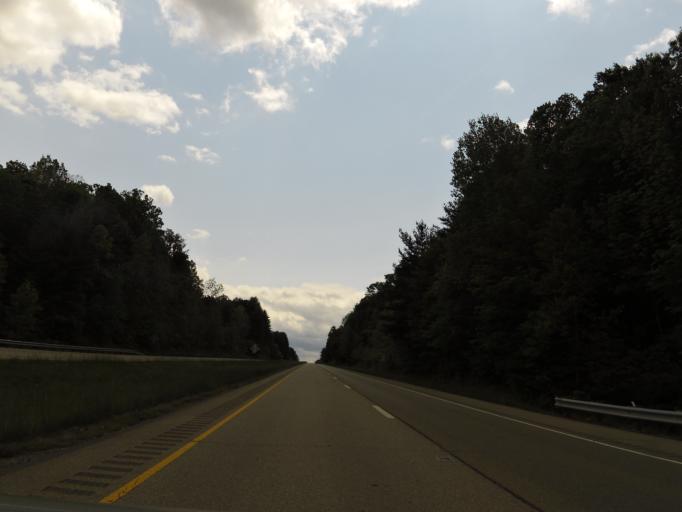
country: US
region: Ohio
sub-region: Meigs County
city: Pomeroy
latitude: 39.1116
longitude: -82.0149
